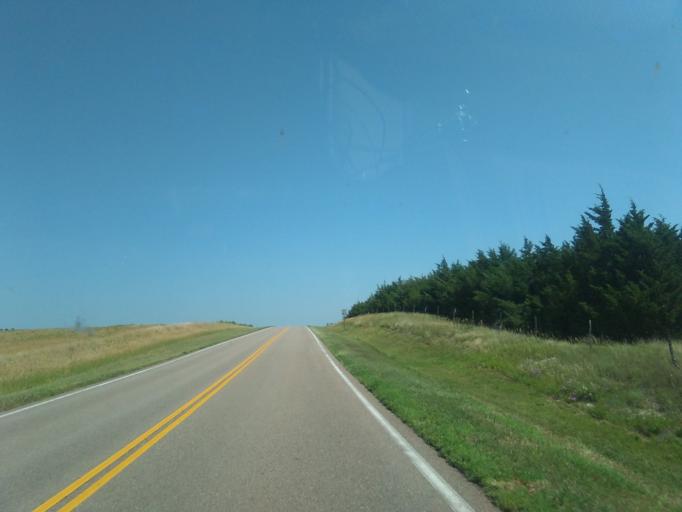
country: US
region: Nebraska
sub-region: Dundy County
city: Benkelman
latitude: 39.9030
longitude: -101.5412
